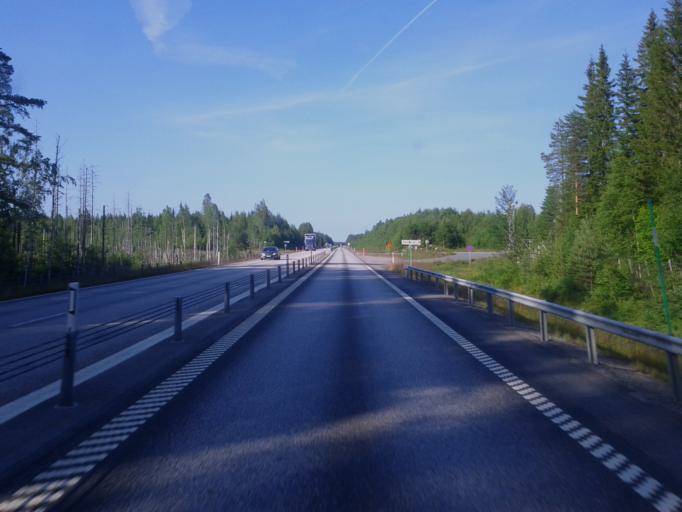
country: SE
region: Vaesterbotten
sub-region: Umea Kommun
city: Saevar
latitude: 63.9682
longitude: 20.7078
